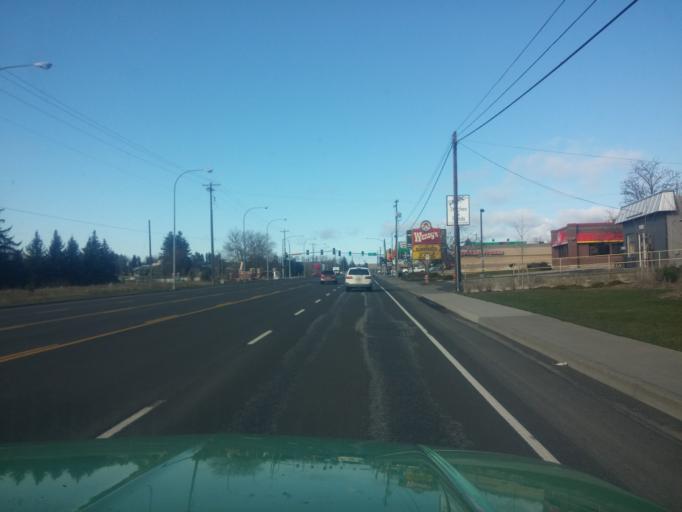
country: US
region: Idaho
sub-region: Latah County
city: Moscow
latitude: 46.7332
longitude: -117.0142
